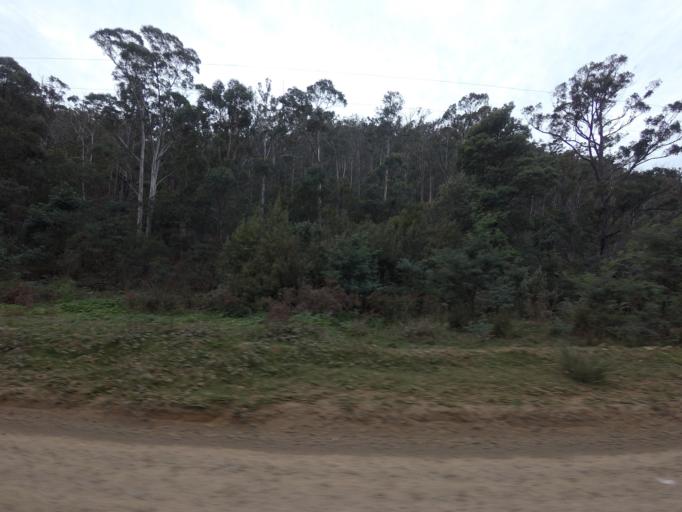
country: AU
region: Tasmania
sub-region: Derwent Valley
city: New Norfolk
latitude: -42.5896
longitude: 147.0259
